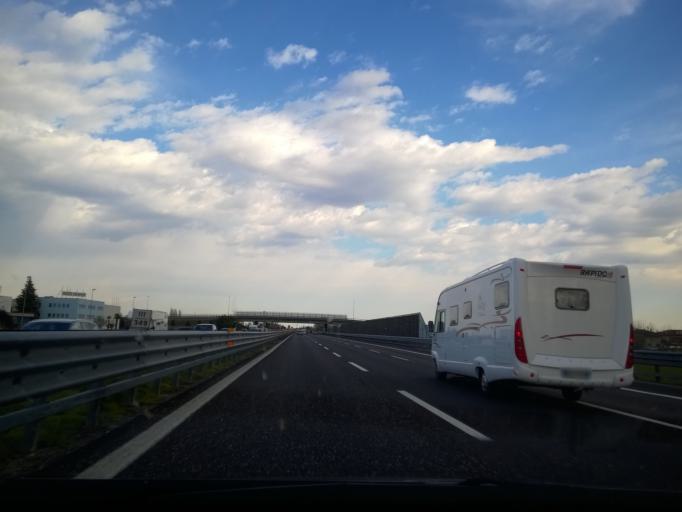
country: IT
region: Veneto
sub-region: Provincia di Padova
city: Ronchi di Campanile
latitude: 45.4611
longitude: 11.7747
